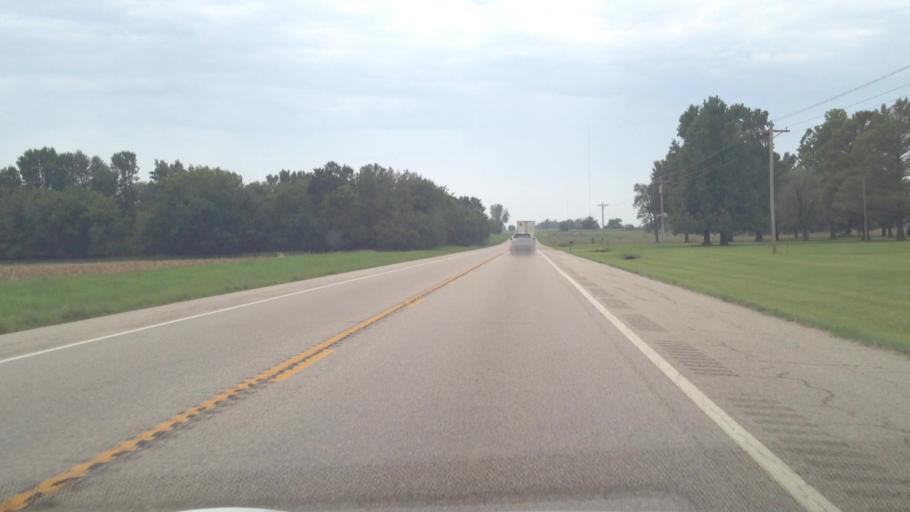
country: US
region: Missouri
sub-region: Jasper County
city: Carl Junction
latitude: 37.2497
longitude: -94.7051
